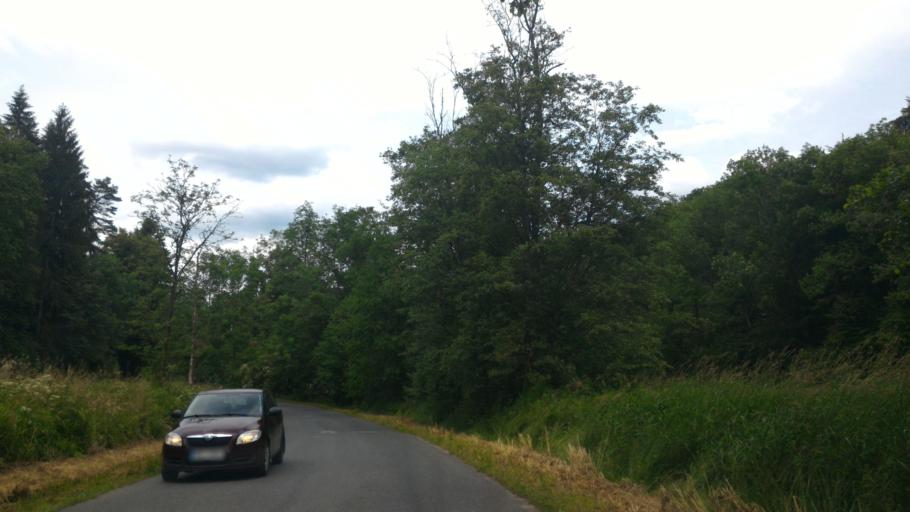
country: CZ
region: Central Bohemia
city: Mseno
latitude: 50.4205
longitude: 14.5758
